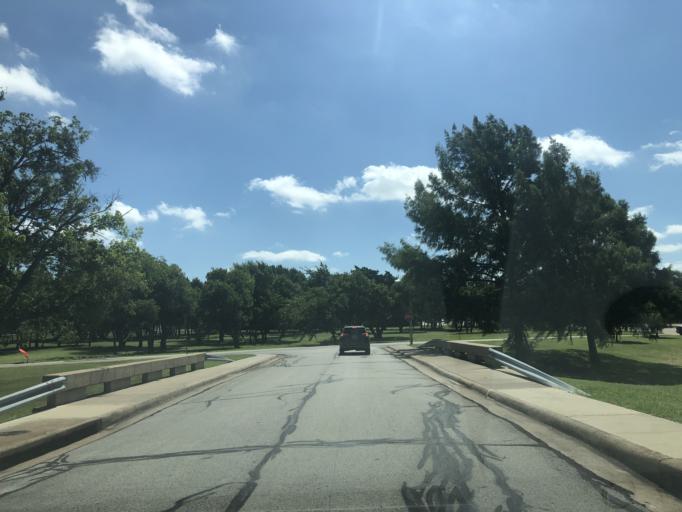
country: US
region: Texas
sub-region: Dallas County
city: Duncanville
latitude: 32.6480
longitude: -96.9292
